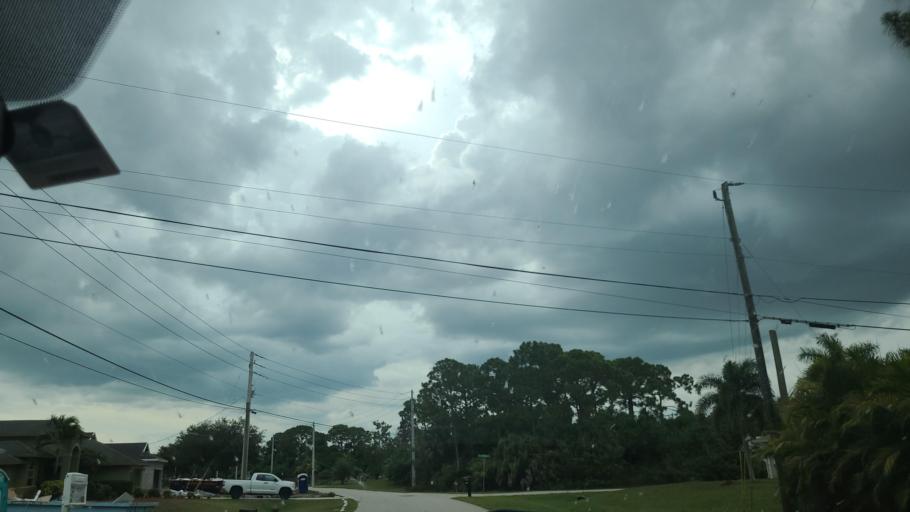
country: US
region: Florida
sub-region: Saint Lucie County
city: Port Saint Lucie
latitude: 27.2495
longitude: -80.4068
